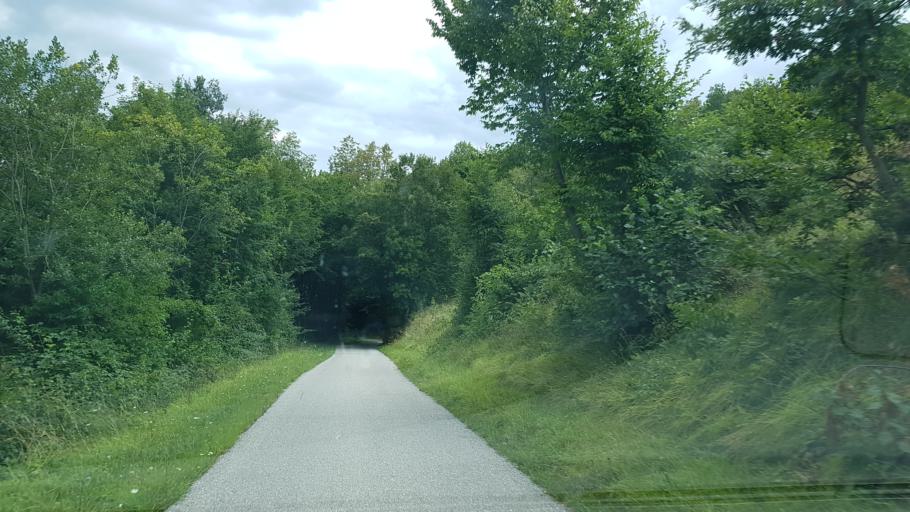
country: SI
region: Kanal
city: Deskle
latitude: 46.0678
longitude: 13.5724
